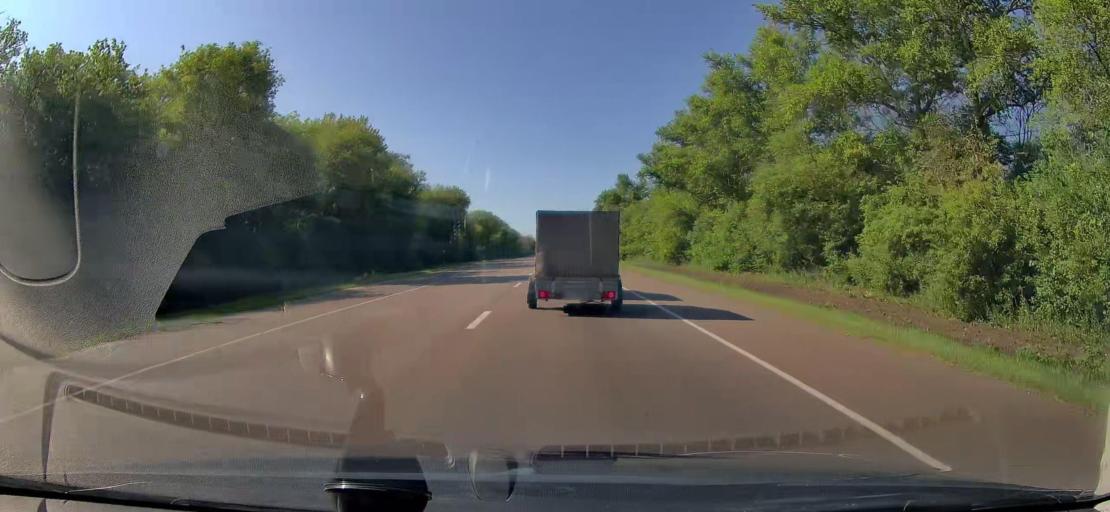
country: RU
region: Orjol
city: Kromy
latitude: 52.6100
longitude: 35.7626
